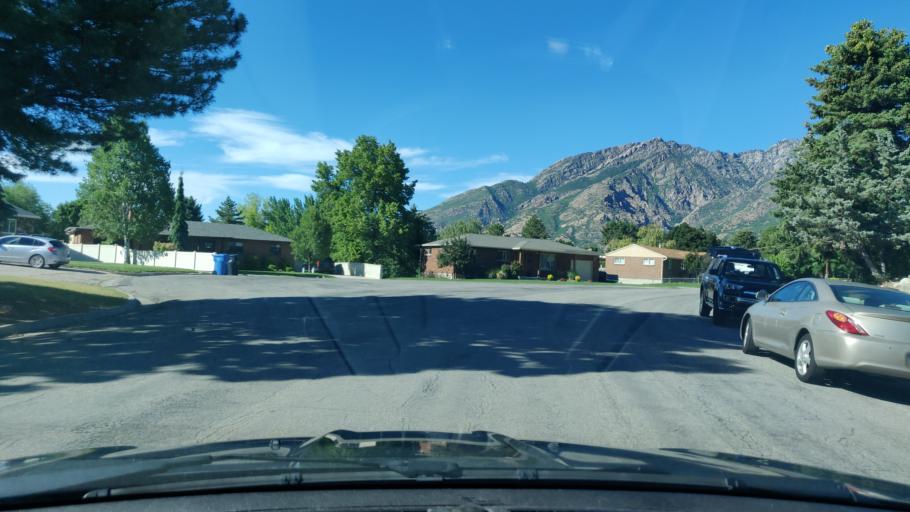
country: US
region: Utah
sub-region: Salt Lake County
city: Cottonwood Heights
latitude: 40.6111
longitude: -111.8147
